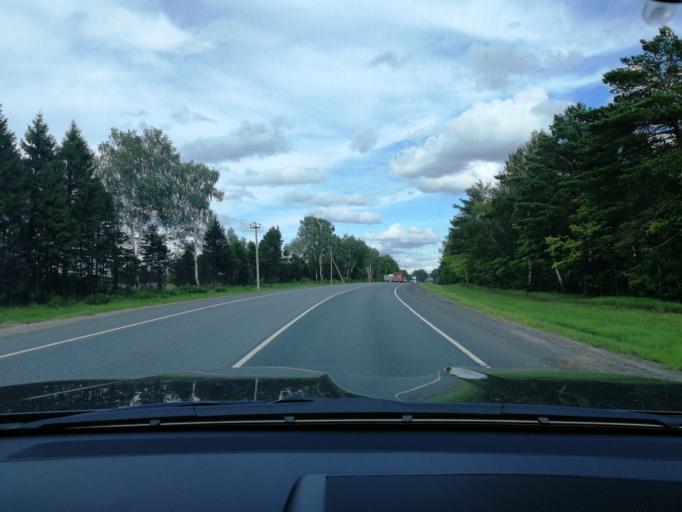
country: RU
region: Moskovskaya
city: Mikhnevo
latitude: 55.0723
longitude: 37.8161
